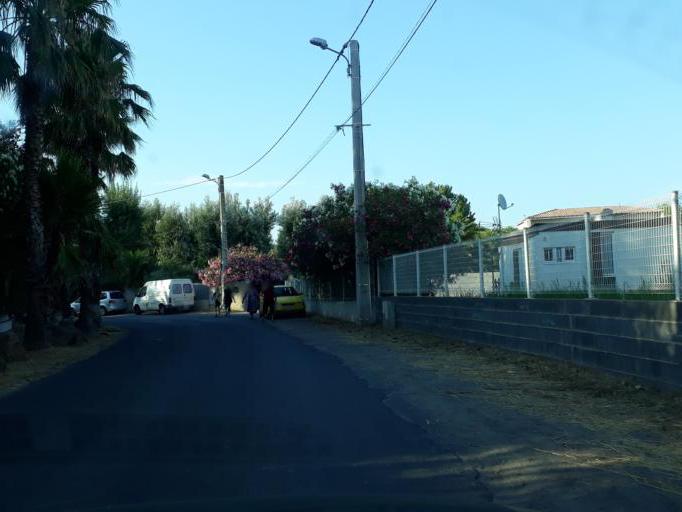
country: FR
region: Languedoc-Roussillon
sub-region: Departement de l'Herault
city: Agde
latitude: 43.2816
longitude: 3.4742
